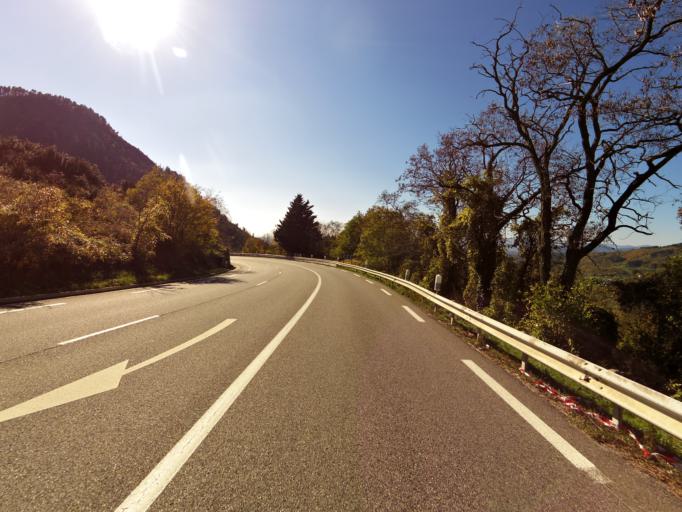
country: FR
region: Rhone-Alpes
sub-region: Departement de l'Ardeche
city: Saint-Priest
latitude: 44.7102
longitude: 4.4881
